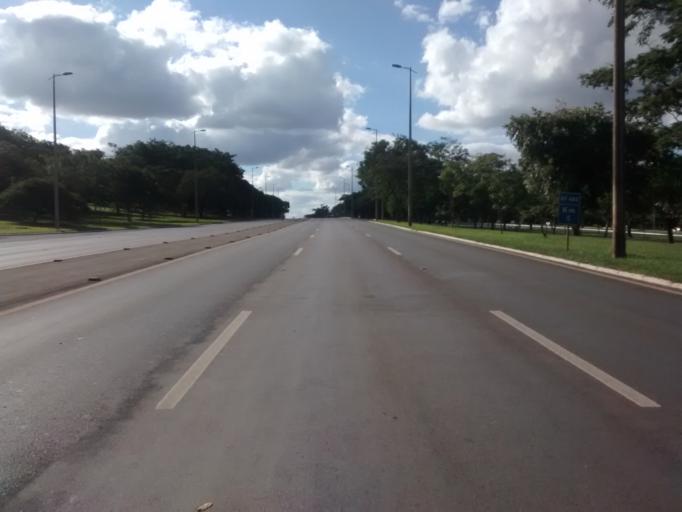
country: BR
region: Federal District
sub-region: Brasilia
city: Brasilia
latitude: -15.7748
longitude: -47.8811
